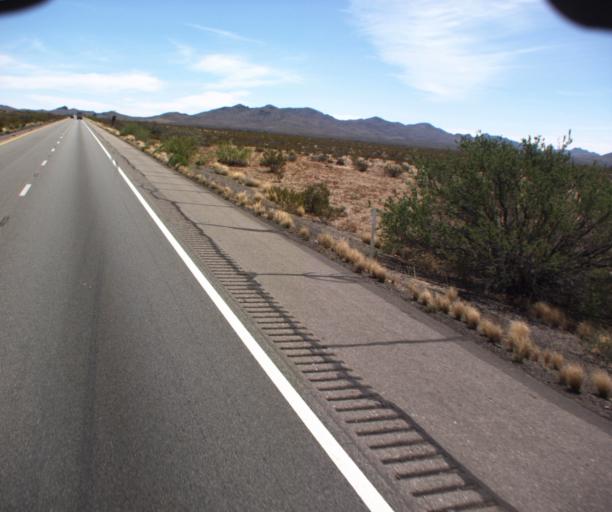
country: US
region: New Mexico
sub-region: Hidalgo County
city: Lordsburg
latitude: 32.2317
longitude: -109.0670
